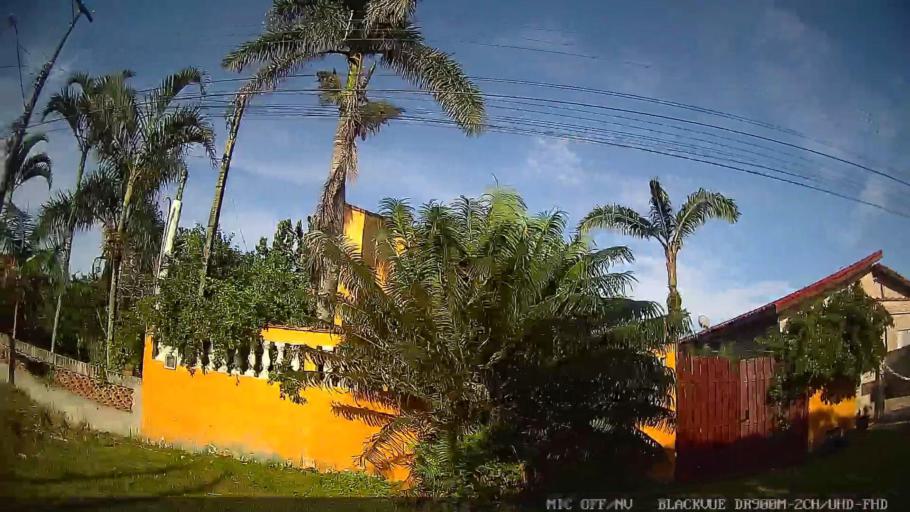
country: BR
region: Sao Paulo
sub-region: Iguape
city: Iguape
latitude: -24.7604
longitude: -47.5733
